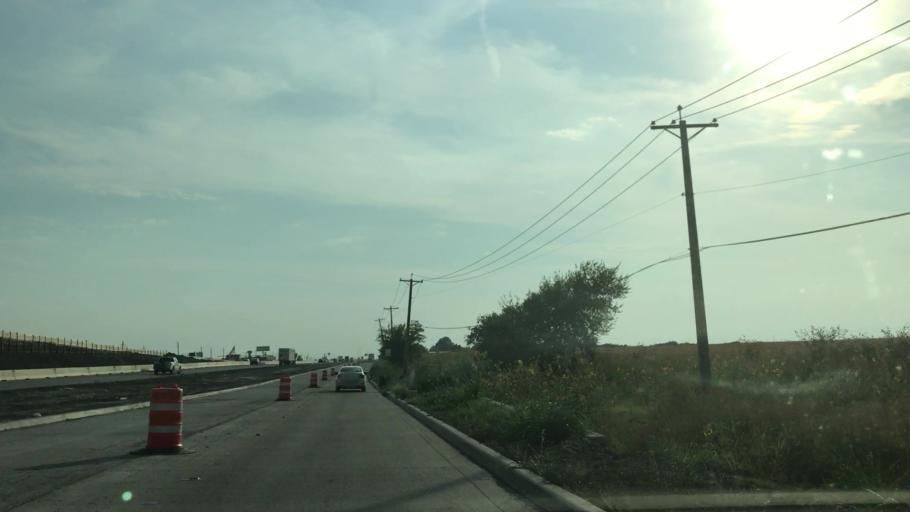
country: US
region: Texas
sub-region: Rockwall County
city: Rockwall
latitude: 32.9197
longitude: -96.4199
